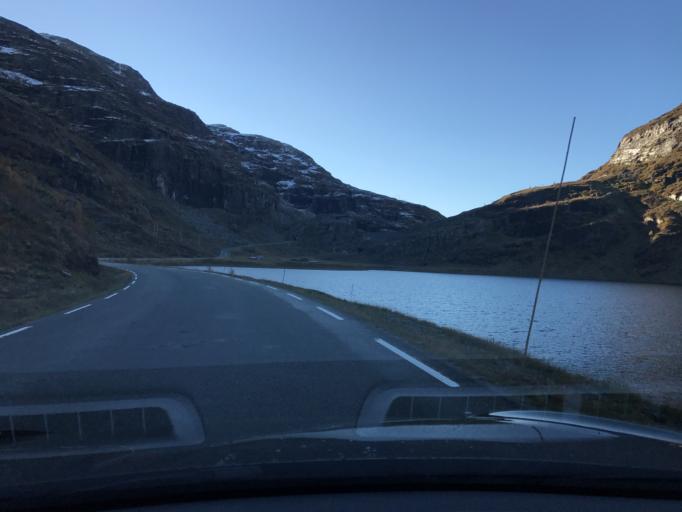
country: NO
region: Sogn og Fjordane
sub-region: Laerdal
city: Laerdalsoyri
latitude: 60.8071
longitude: 7.5596
